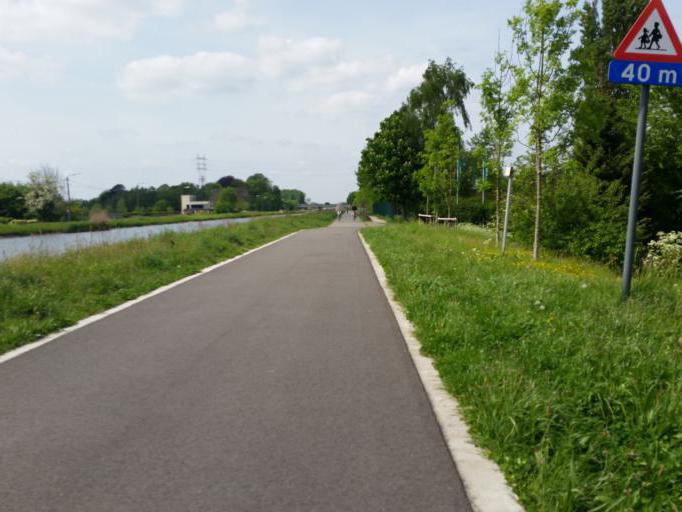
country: BE
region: Flanders
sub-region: Provincie Antwerpen
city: Mechelen
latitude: 51.0296
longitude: 4.4598
